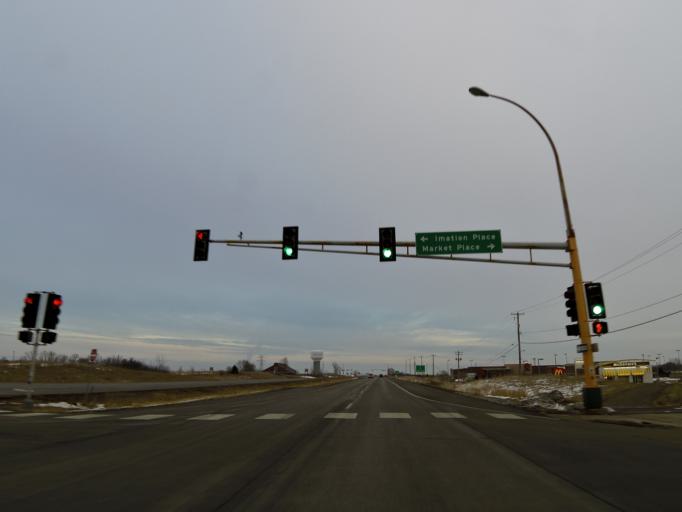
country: US
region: Minnesota
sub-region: Washington County
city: Oakdale
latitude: 44.9975
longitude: -92.9502
